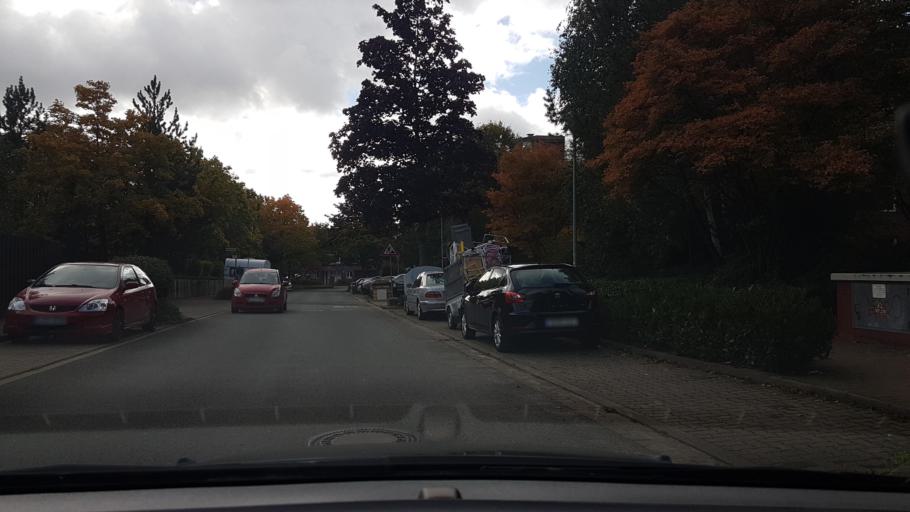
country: DE
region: Lower Saxony
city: Ronnenberg
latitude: 52.3436
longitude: 9.6783
